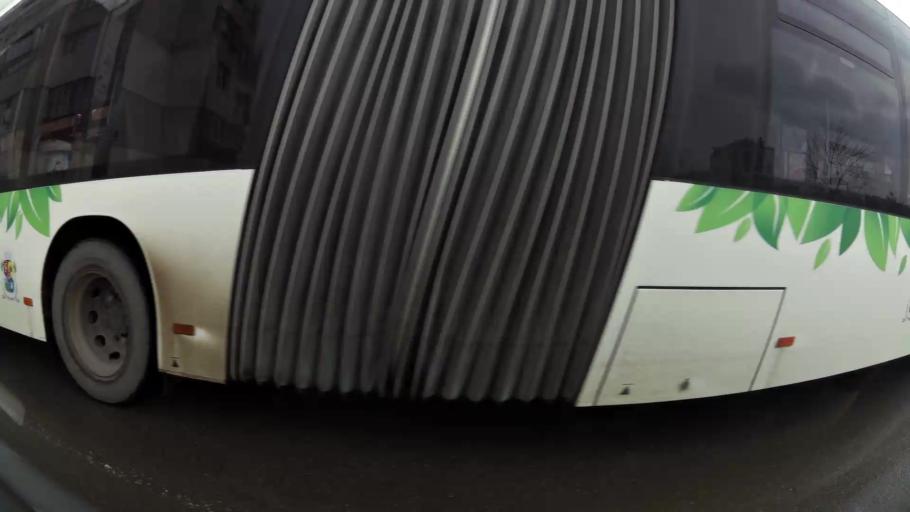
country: BG
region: Sofia-Capital
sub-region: Stolichna Obshtina
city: Sofia
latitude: 42.7121
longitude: 23.3798
